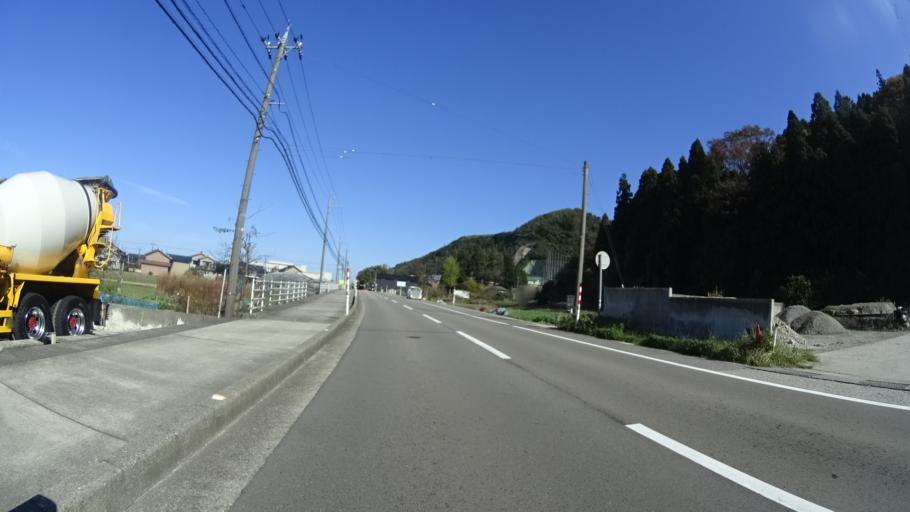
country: JP
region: Ishikawa
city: Tsurugi-asahimachi
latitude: 36.4879
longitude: 136.6180
